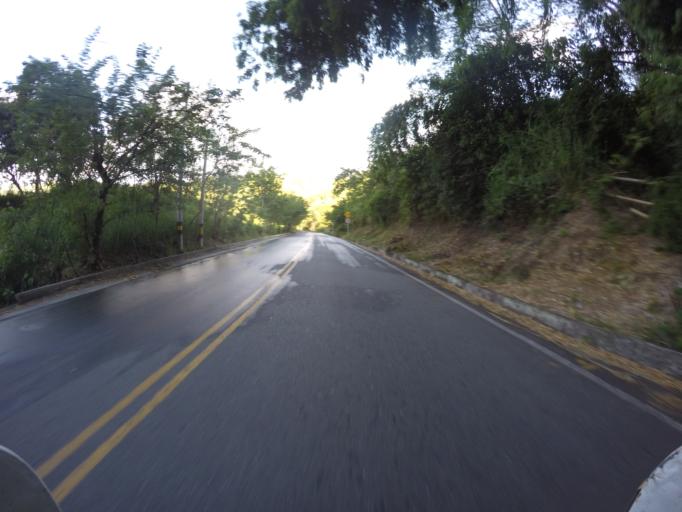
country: CO
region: Valle del Cauca
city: Cartago
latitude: 4.7192
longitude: -75.8622
